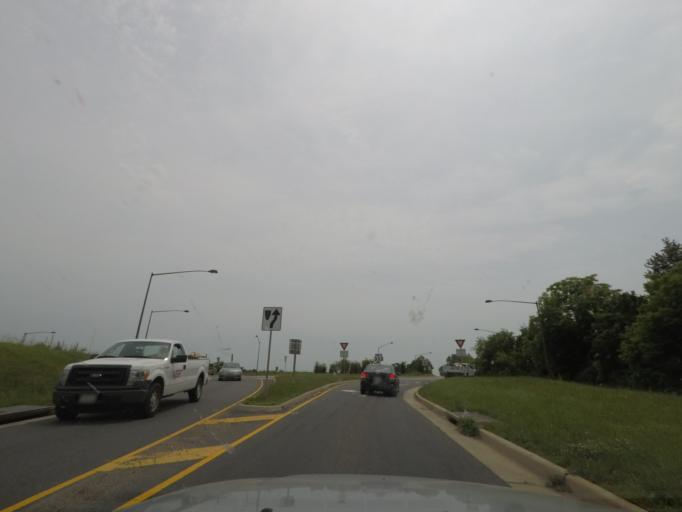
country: US
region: Virginia
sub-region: Prince William County
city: Bull Run Mountain Estates
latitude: 38.9652
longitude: -77.6225
